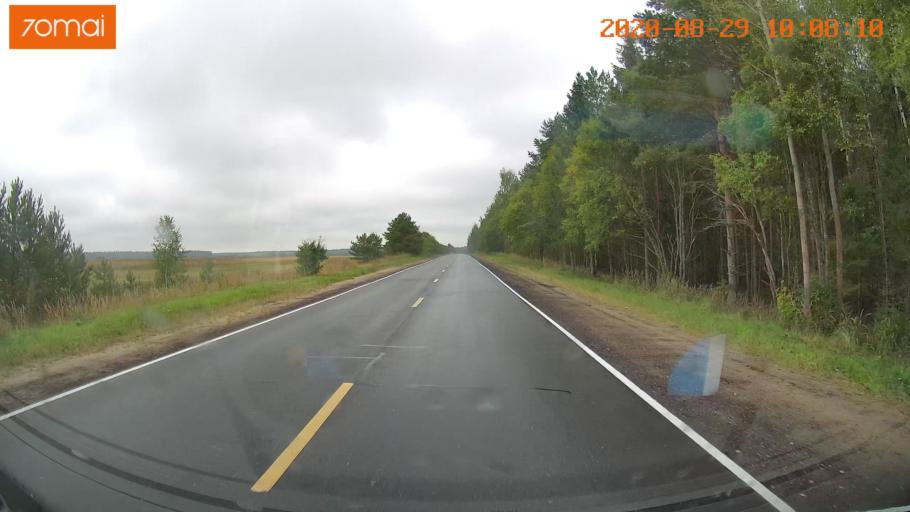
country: RU
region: Ivanovo
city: Kuznechikha
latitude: 57.3769
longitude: 42.5833
